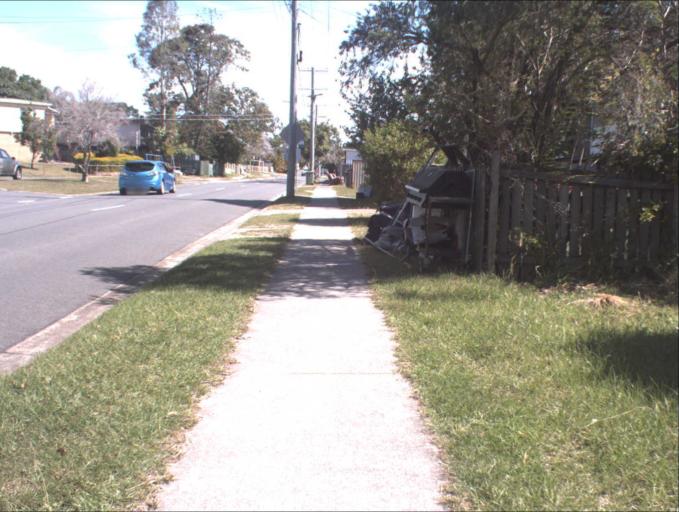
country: AU
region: Queensland
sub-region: Logan
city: Logan City
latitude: -27.6440
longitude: 153.1284
